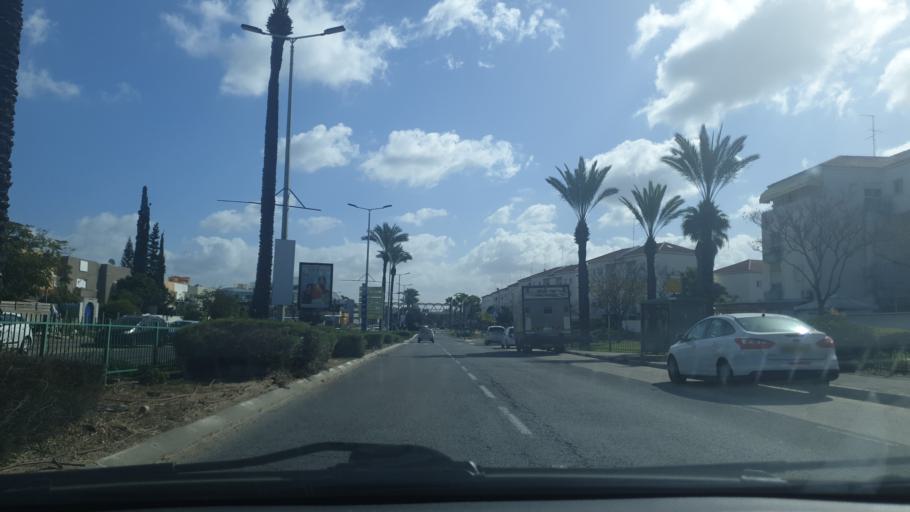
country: IL
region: Haifa
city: Qesarya
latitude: 32.5022
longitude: 34.9231
